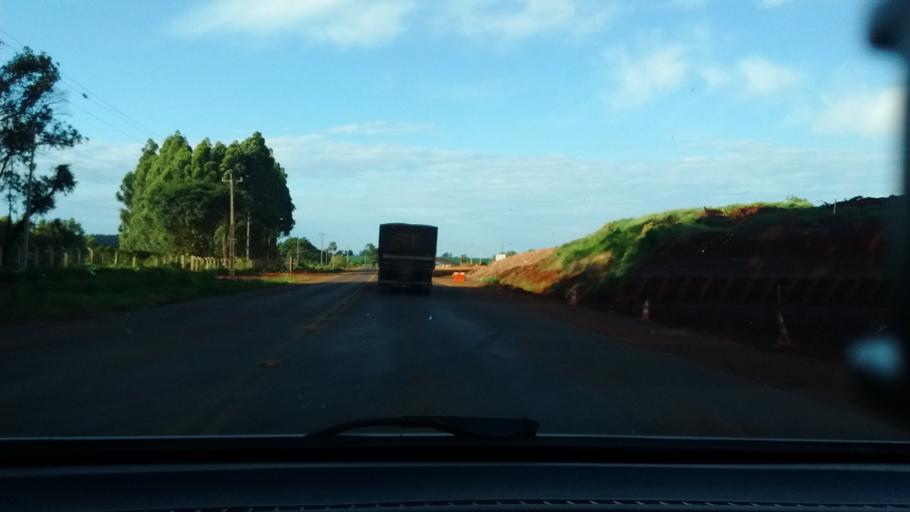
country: BR
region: Parana
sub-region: Cascavel
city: Cascavel
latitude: -25.1460
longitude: -53.5905
